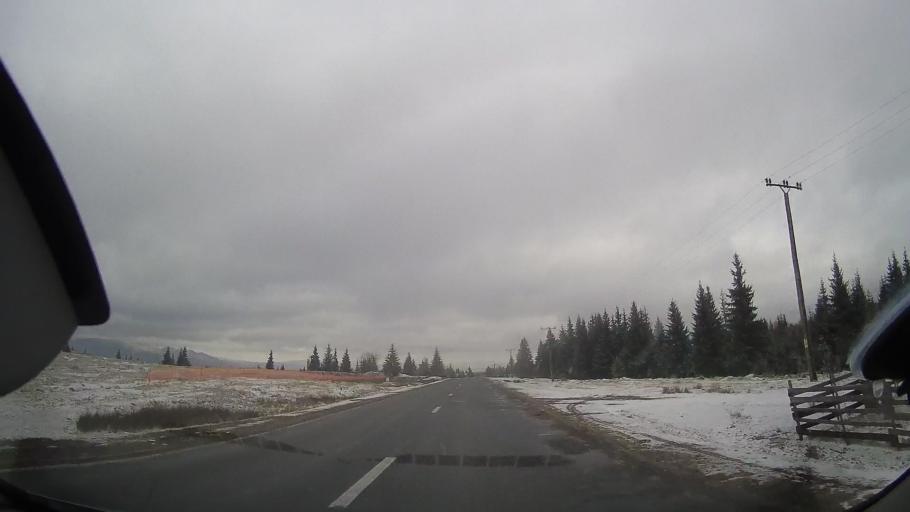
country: RO
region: Cluj
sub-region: Comuna Belis
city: Belis
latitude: 46.6989
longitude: 23.0364
